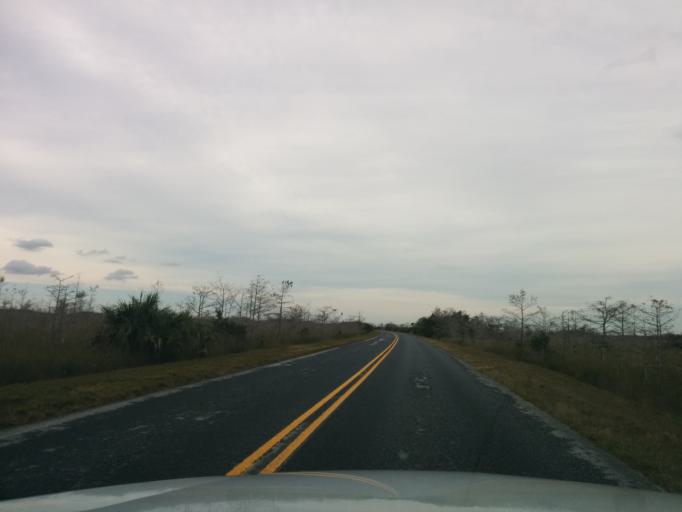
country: US
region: Florida
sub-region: Miami-Dade County
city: Florida City
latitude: 25.4325
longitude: -80.7616
